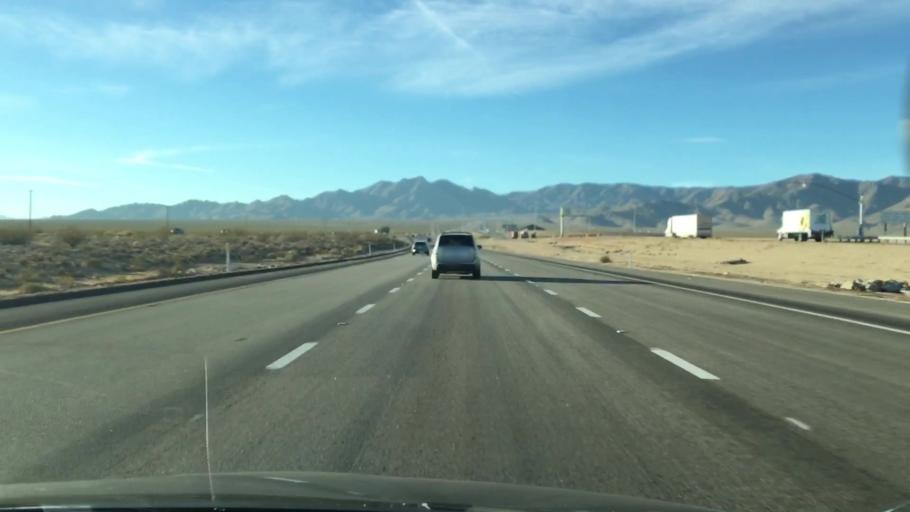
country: US
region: Nevada
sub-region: Clark County
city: Sandy Valley
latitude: 35.5118
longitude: -115.4330
